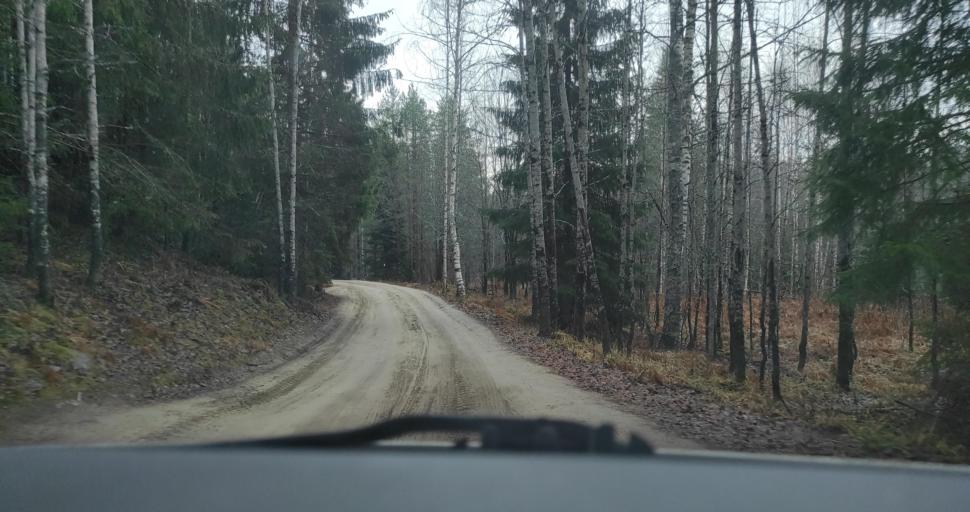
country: RU
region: Republic of Karelia
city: Pitkyaranta
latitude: 61.7486
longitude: 31.3970
